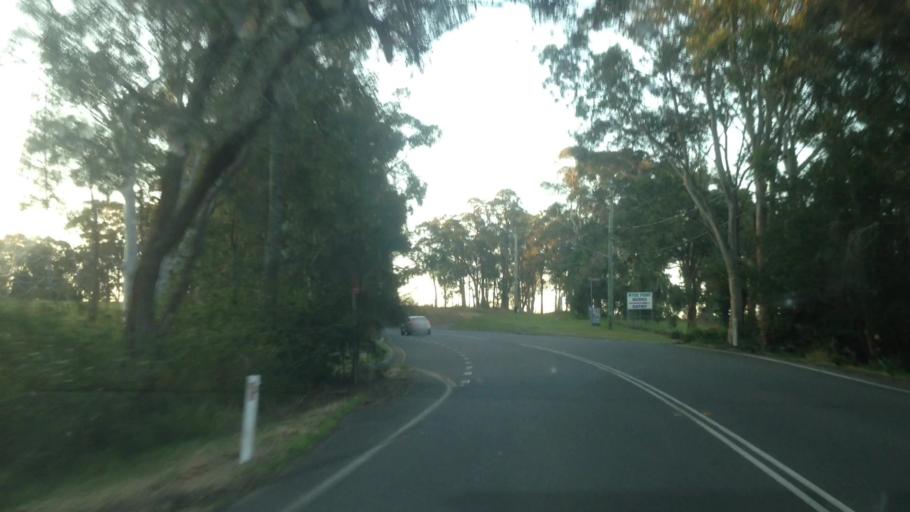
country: AU
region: New South Wales
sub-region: Wyong Shire
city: Kingfisher Shores
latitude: -33.1533
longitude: 151.5252
